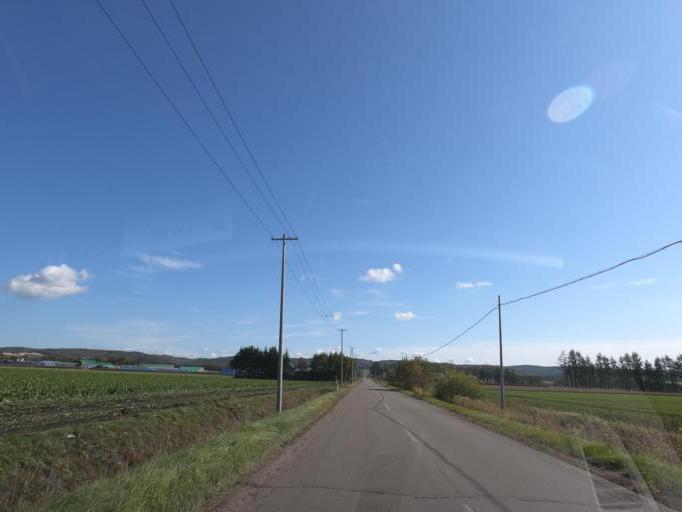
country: JP
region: Hokkaido
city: Otofuke
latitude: 43.0610
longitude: 143.2640
